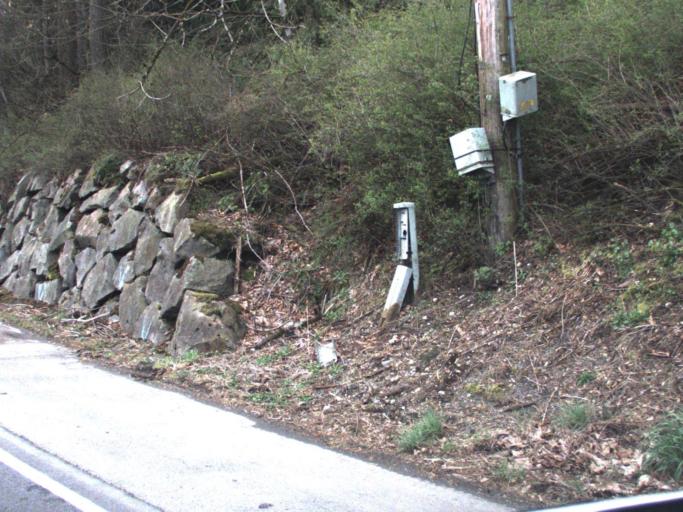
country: US
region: Washington
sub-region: King County
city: Lea Hill
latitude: 47.2791
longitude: -122.1636
